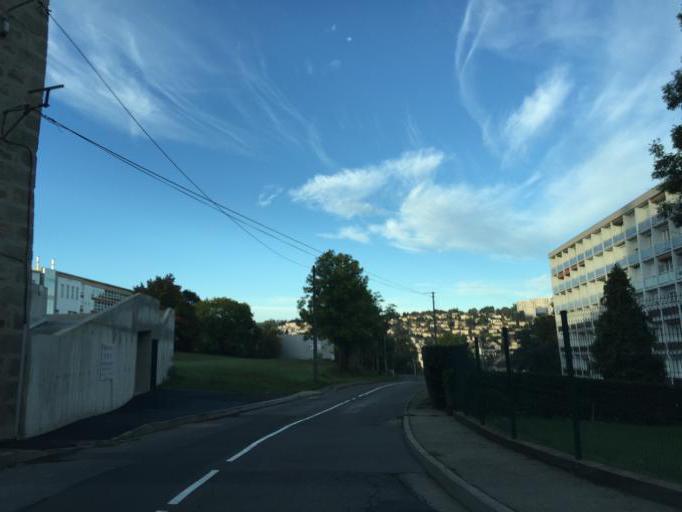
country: FR
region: Rhone-Alpes
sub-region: Departement de la Loire
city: Saint-Priest-en-Jarez
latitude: 45.4653
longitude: 4.3753
